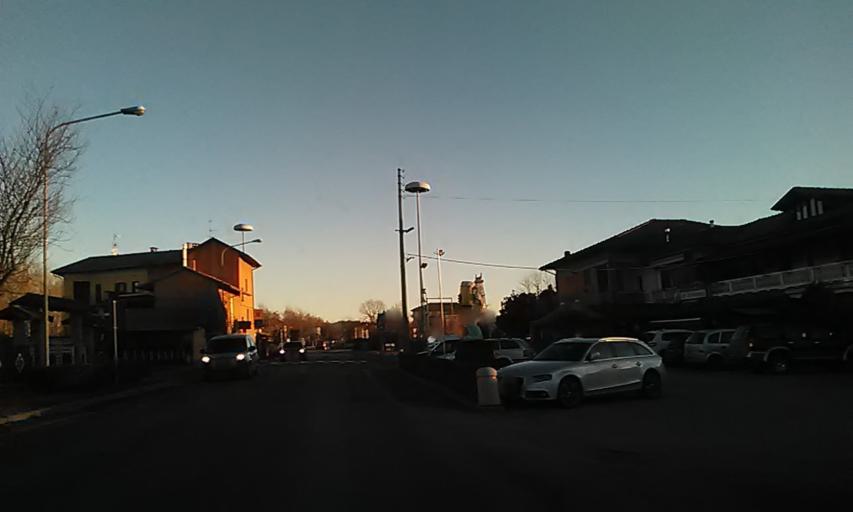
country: IT
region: Piedmont
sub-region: Provincia di Biella
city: Brusnengo
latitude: 45.5624
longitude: 8.2427
